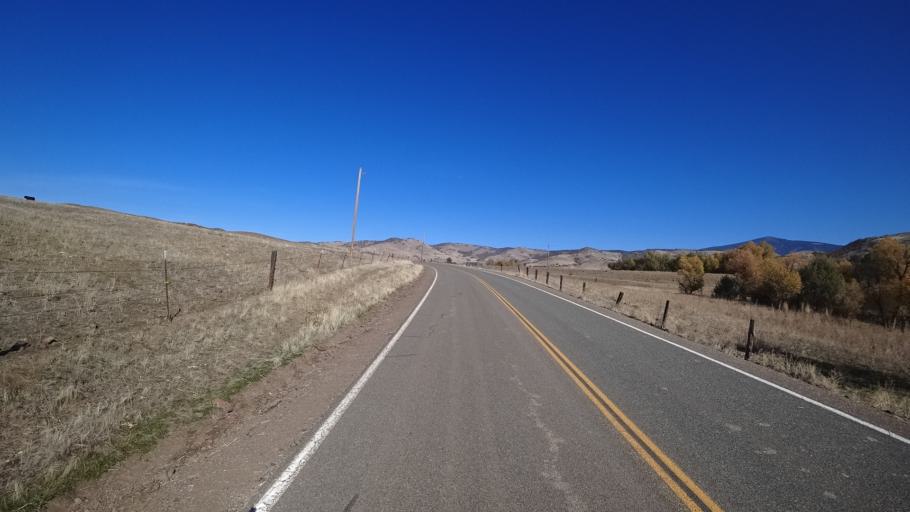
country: US
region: California
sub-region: Siskiyou County
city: Montague
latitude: 41.8094
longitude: -122.3772
